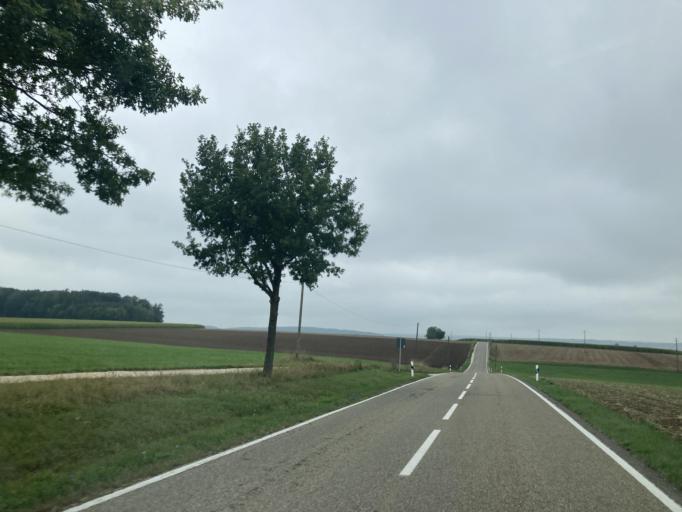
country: DE
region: Bavaria
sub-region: Swabia
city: Bachhagel
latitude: 48.6031
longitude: 10.3089
